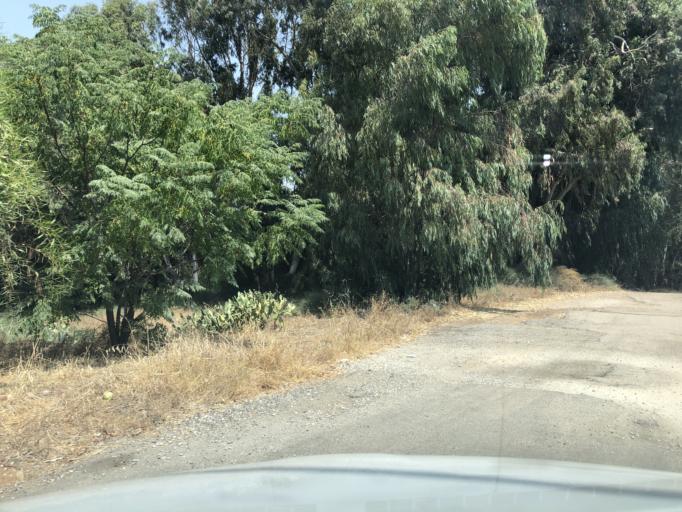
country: IL
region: Central District
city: Ganne Tiqwa
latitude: 32.0684
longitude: 34.8748
